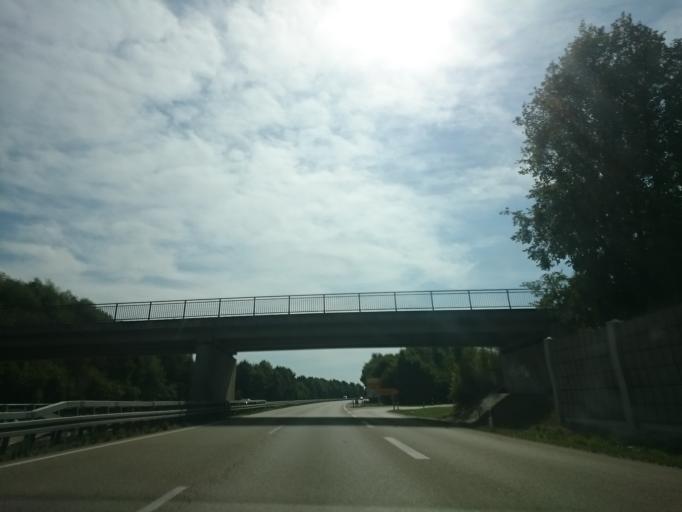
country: DE
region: Bavaria
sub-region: Swabia
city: Asbach-Baumenheim
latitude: 48.6844
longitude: 10.8212
